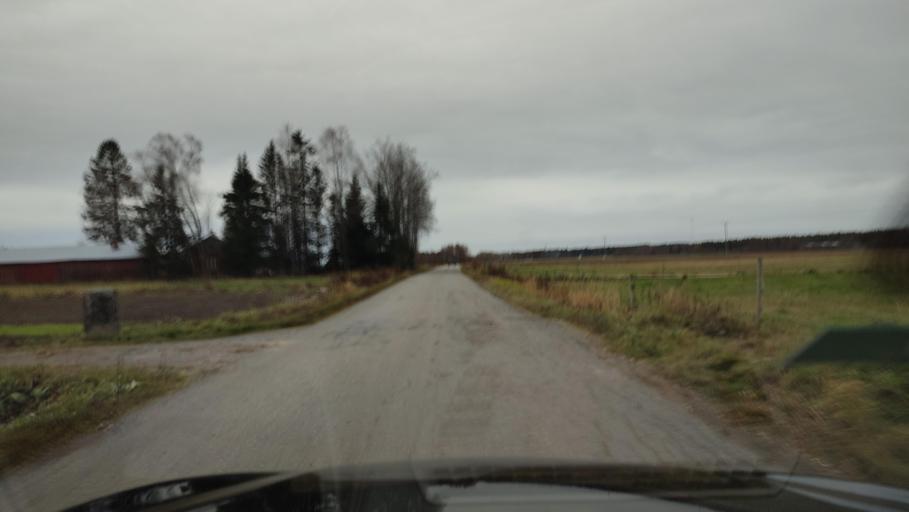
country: FI
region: Ostrobothnia
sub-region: Sydosterbotten
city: Naerpes
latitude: 62.4098
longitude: 21.3979
